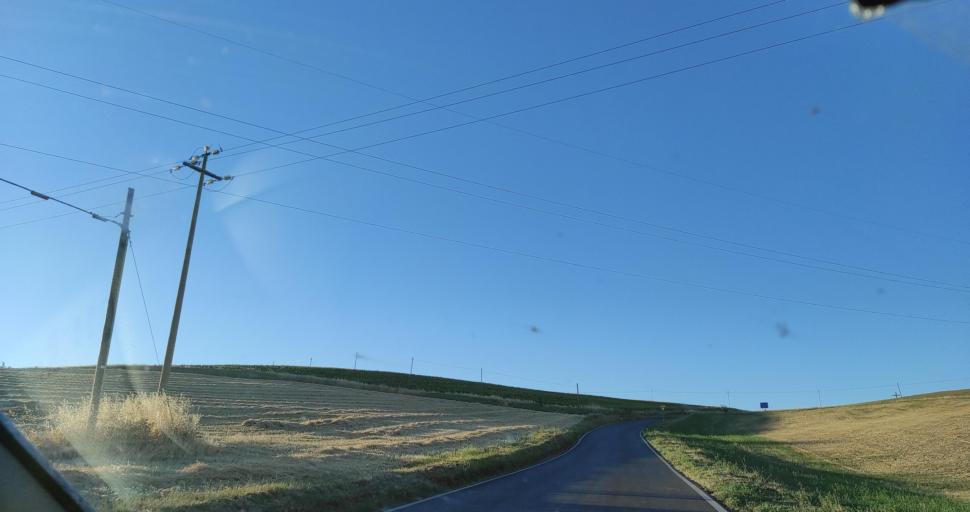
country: IT
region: The Marches
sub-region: Provincia di Macerata
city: Casette Verdini
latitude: 43.2314
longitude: 13.3946
